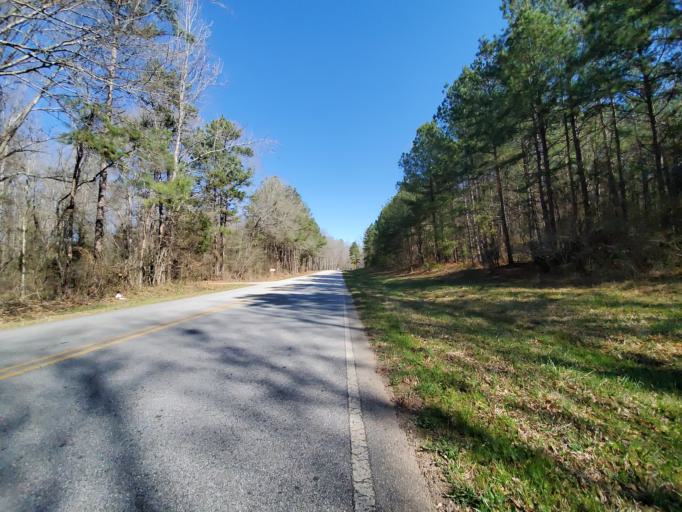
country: US
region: Georgia
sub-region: Oconee County
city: Bogart
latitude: 34.0012
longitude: -83.4954
